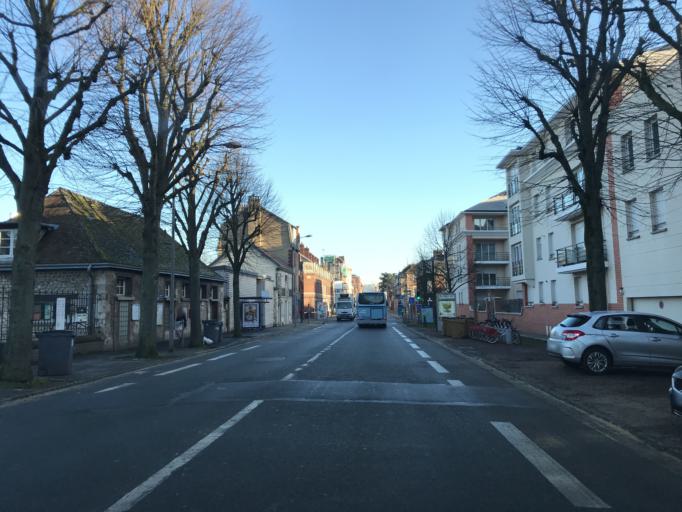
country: FR
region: Haute-Normandie
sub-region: Departement de la Seine-Maritime
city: Sotteville-les-Rouen
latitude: 49.4214
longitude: 1.0795
